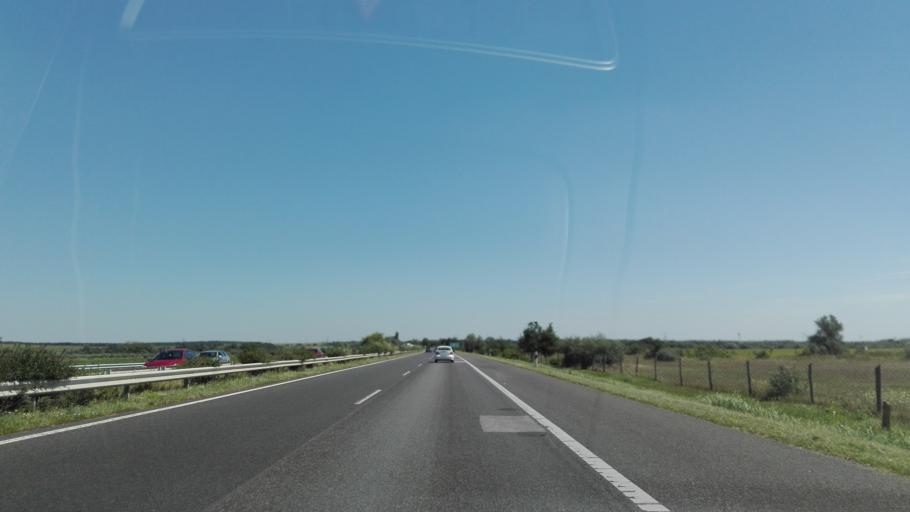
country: HU
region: Fejer
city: Lepseny
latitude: 47.0005
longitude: 18.2124
